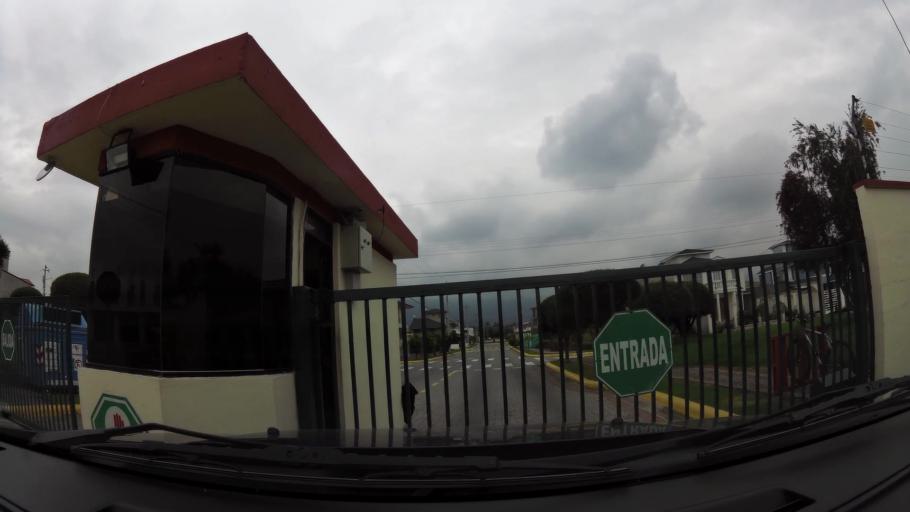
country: EC
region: Pichincha
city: Sangolqui
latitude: -0.3323
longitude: -78.4655
